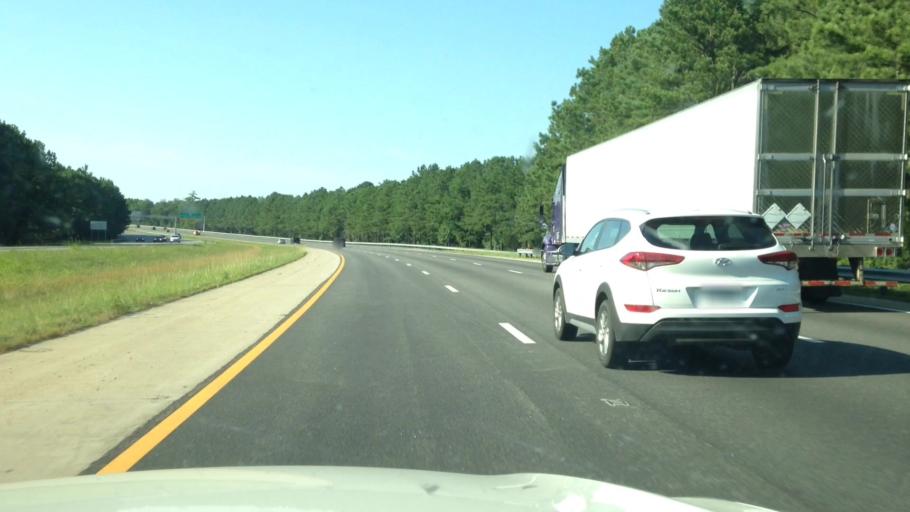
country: US
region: Virginia
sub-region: Chesterfield County
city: Enon
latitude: 37.3455
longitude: -77.3344
